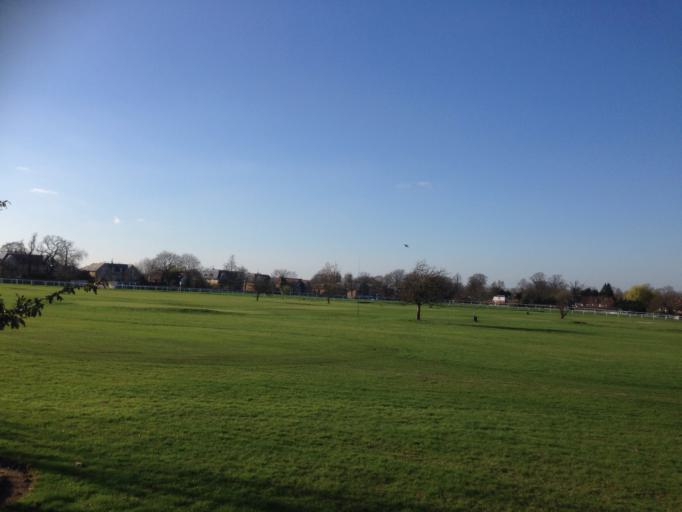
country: GB
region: England
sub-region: Surrey
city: Esher
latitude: 51.3758
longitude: -0.3662
